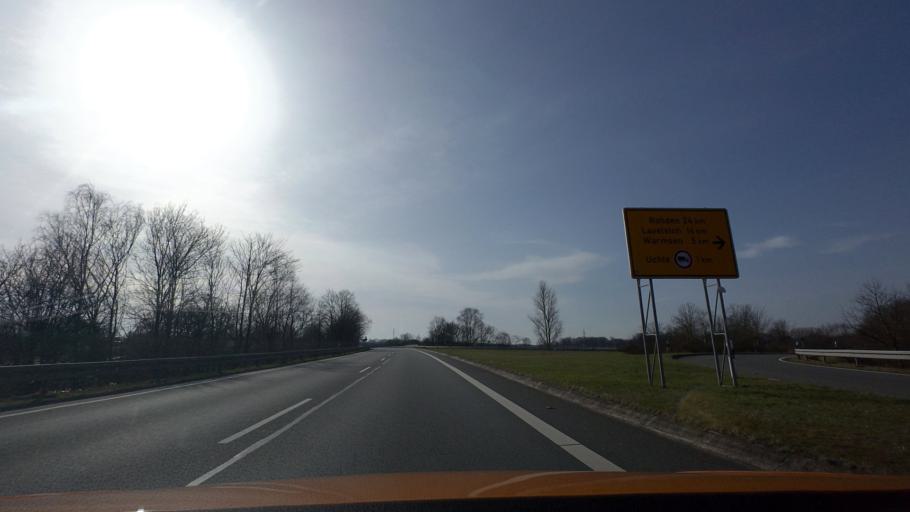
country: DE
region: Lower Saxony
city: Uchte
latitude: 52.4906
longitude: 8.8894
